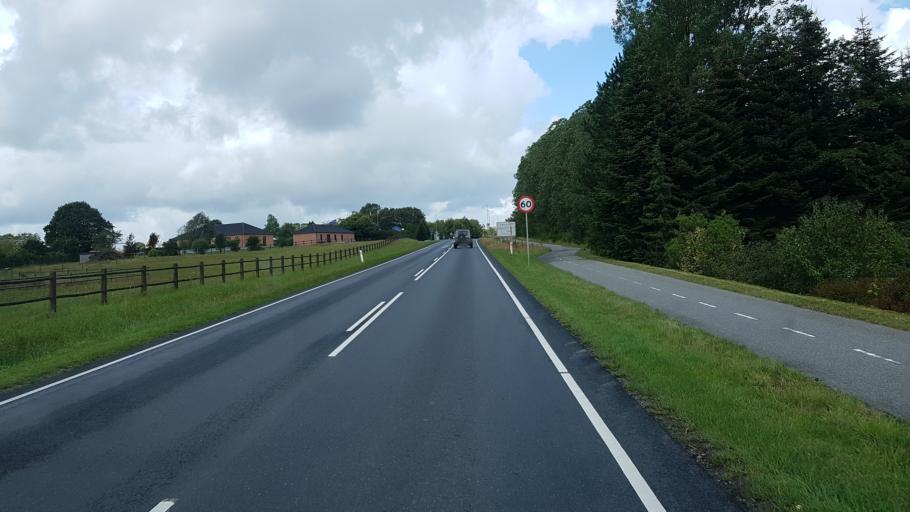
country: DK
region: South Denmark
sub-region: Vejen Kommune
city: Vejen
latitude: 55.5209
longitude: 9.1193
